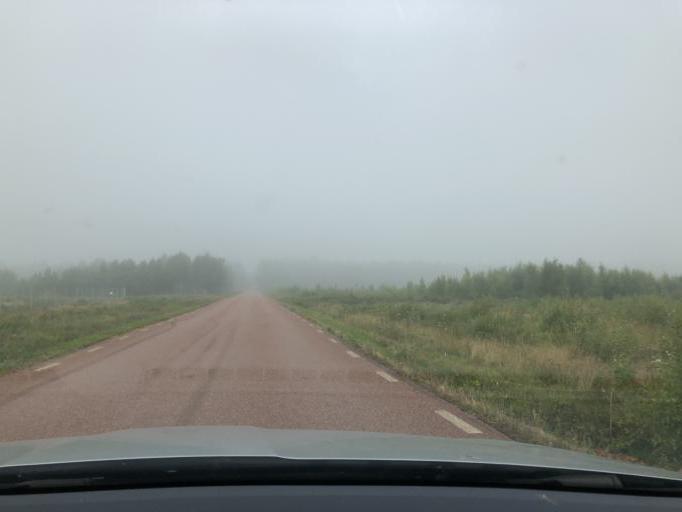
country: SE
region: Dalarna
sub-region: Mora Kommun
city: Mora
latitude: 60.9677
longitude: 14.5033
